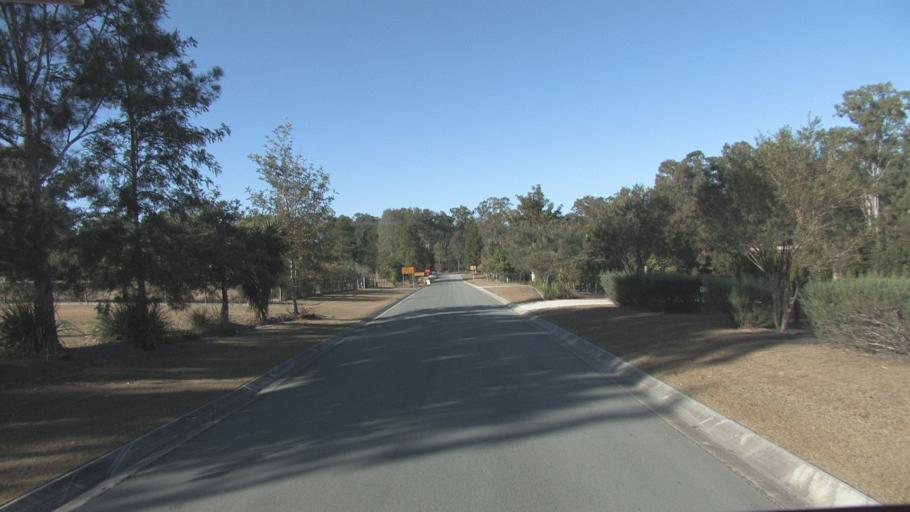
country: AU
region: Queensland
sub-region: Logan
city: Cedar Vale
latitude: -27.8316
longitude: 153.0001
